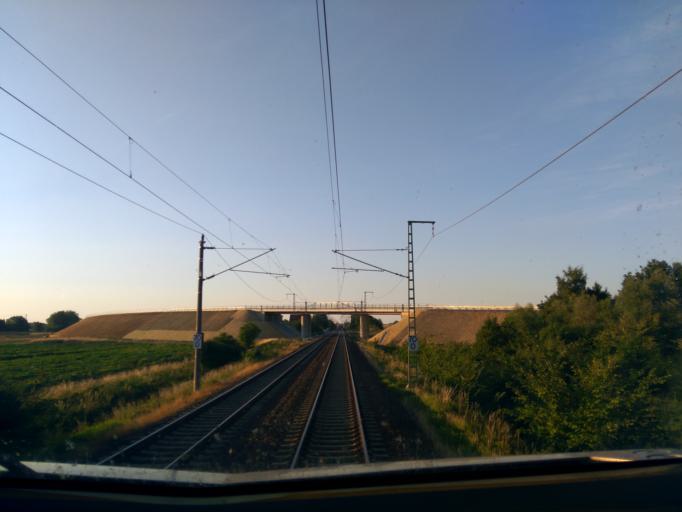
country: DE
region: Mecklenburg-Vorpommern
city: Lewenberg
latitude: 53.6661
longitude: 11.4031
